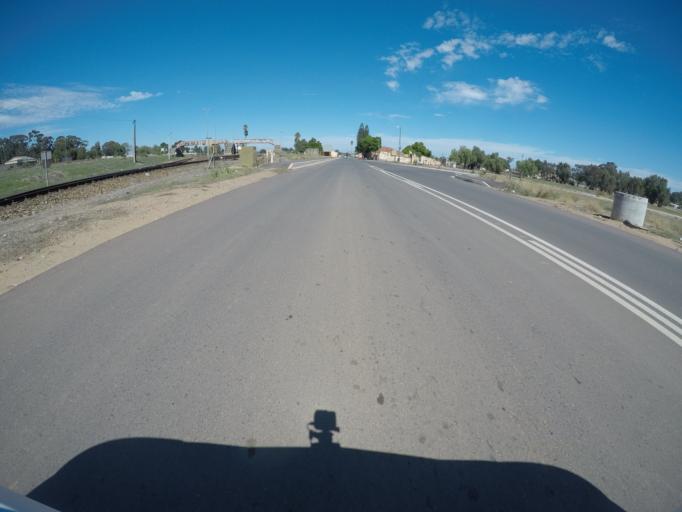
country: ZA
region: Western Cape
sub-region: West Coast District Municipality
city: Malmesbury
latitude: -33.5711
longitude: 18.6471
